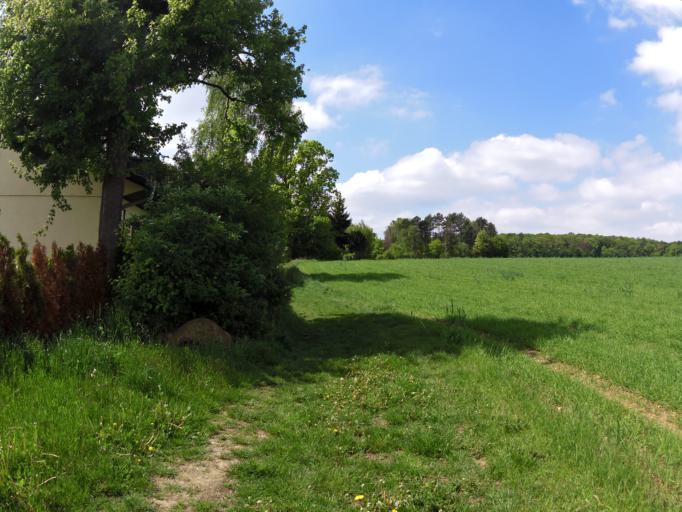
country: DE
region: Bavaria
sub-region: Regierungsbezirk Unterfranken
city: Reichenberg
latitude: 49.7370
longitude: 9.9048
